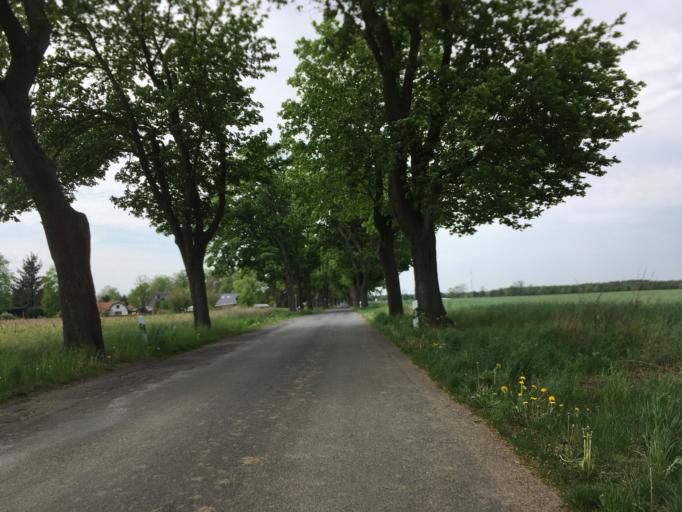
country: DE
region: Brandenburg
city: Rudnitz
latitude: 52.7279
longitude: 13.6412
